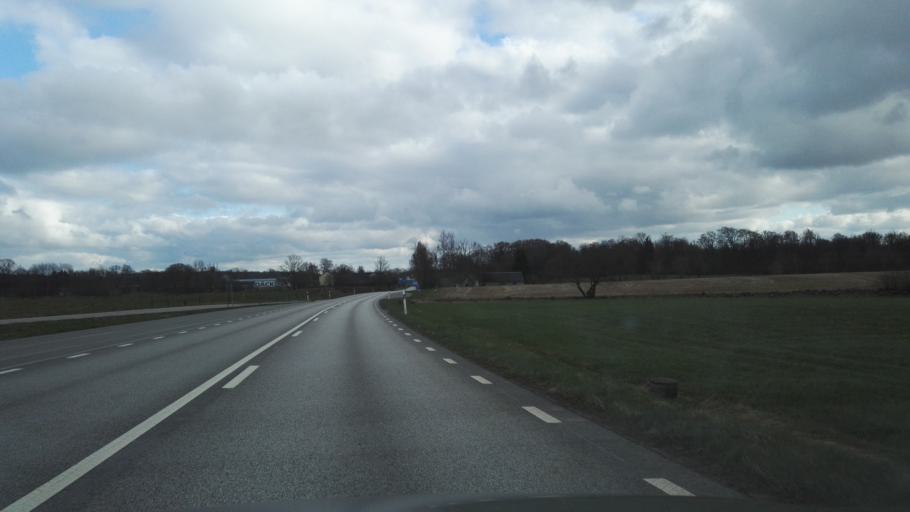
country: SE
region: Skane
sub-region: Sjobo Kommun
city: Sjoebo
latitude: 55.7420
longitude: 13.7003
